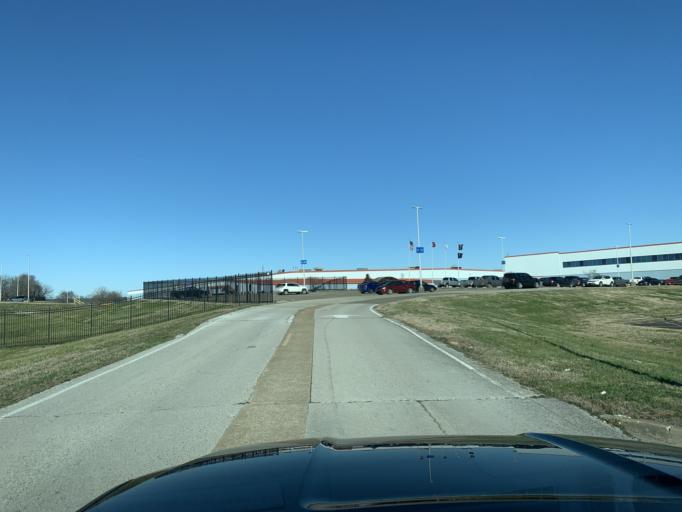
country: US
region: Tennessee
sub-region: Maury County
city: Spring Hill
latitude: 35.7481
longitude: -86.9517
